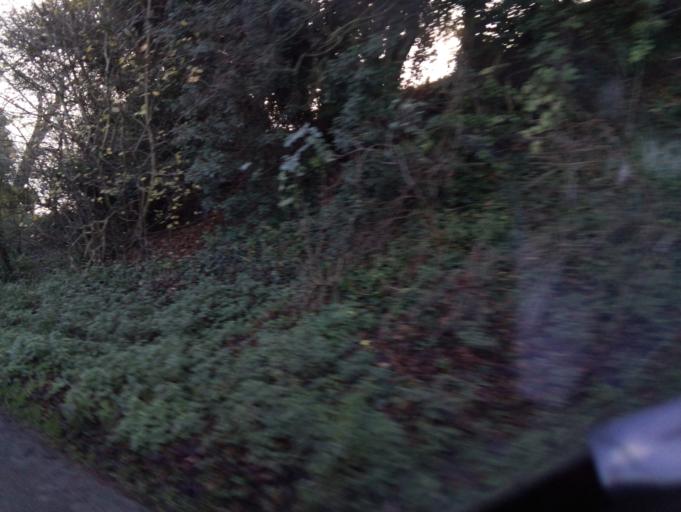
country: GB
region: England
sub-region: Staffordshire
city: Barton under Needwood
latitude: 52.7924
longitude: -1.7023
